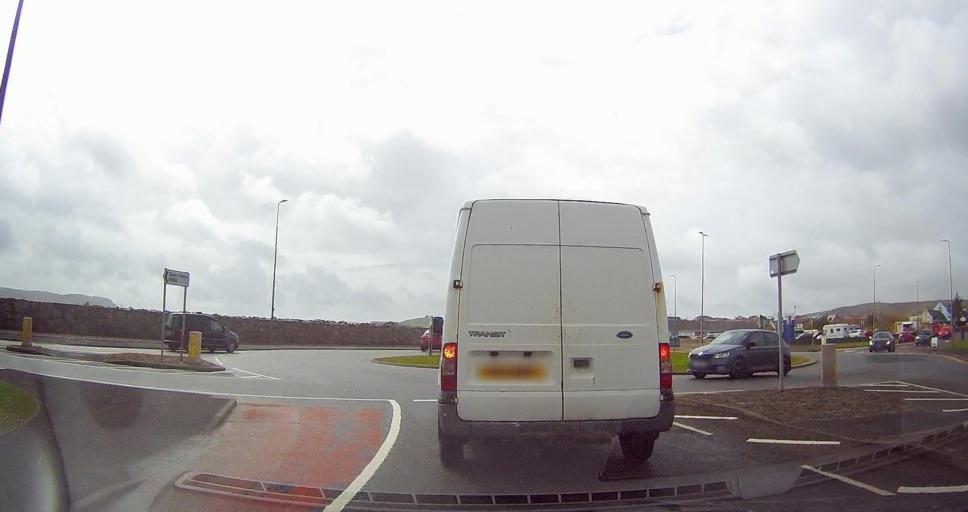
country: GB
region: Scotland
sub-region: Shetland Islands
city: Lerwick
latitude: 60.1494
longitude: -1.1607
